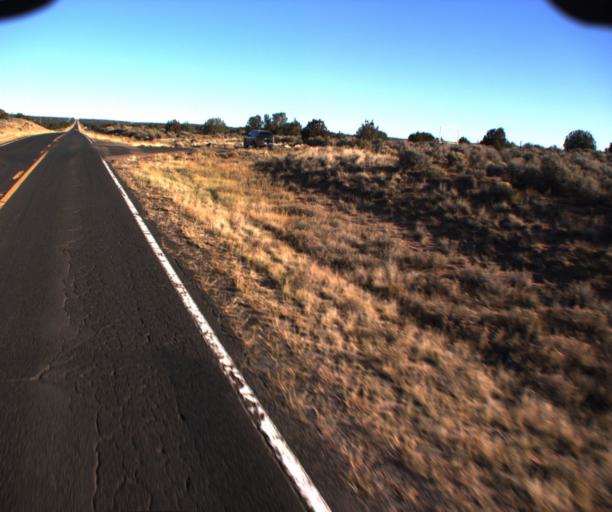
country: US
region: Arizona
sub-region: Apache County
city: Ganado
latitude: 35.5336
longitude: -109.5286
